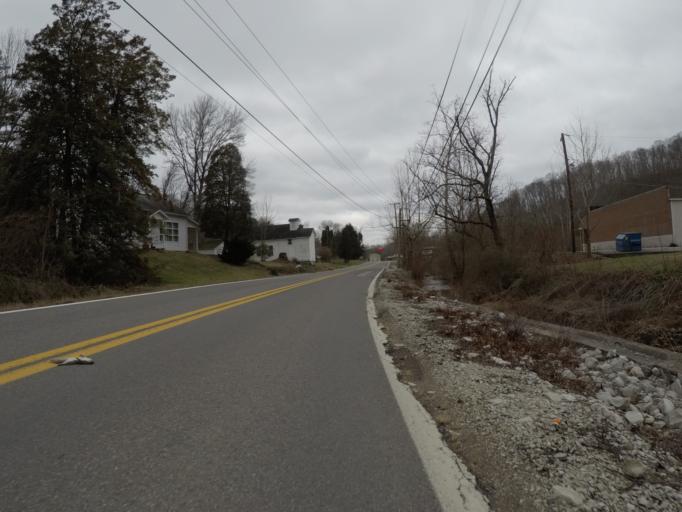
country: US
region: West Virginia
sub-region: Cabell County
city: Barboursville
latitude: 38.4274
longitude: -82.2917
